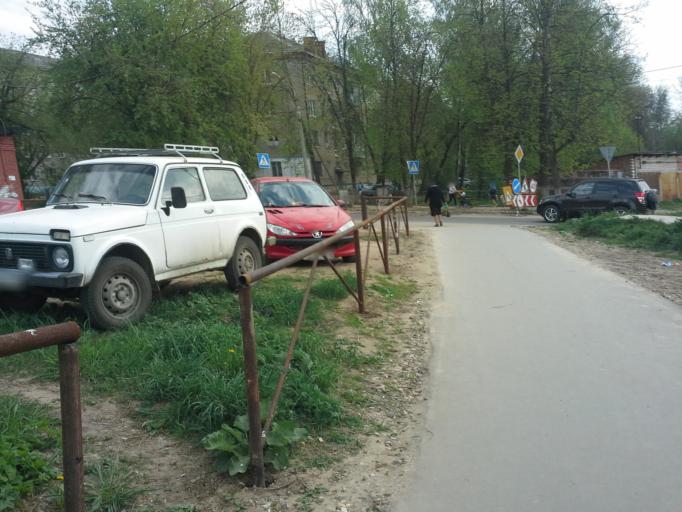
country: RU
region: Moskovskaya
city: Sergiyev Posad
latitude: 56.3166
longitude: 38.1439
